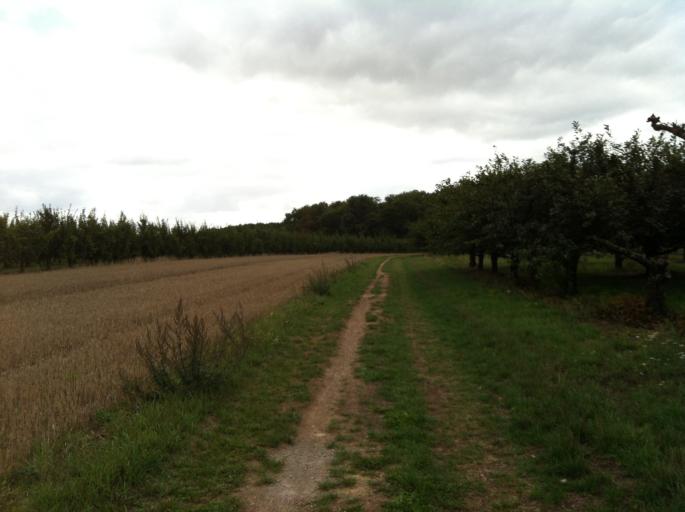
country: DE
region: Rheinland-Pfalz
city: Ober-Olm
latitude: 49.9705
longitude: 8.1775
